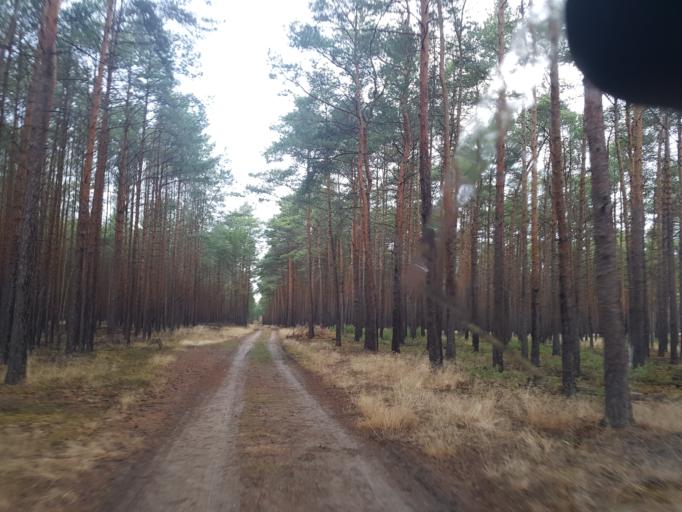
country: DE
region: Brandenburg
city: Finsterwalde
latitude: 51.6407
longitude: 13.6609
